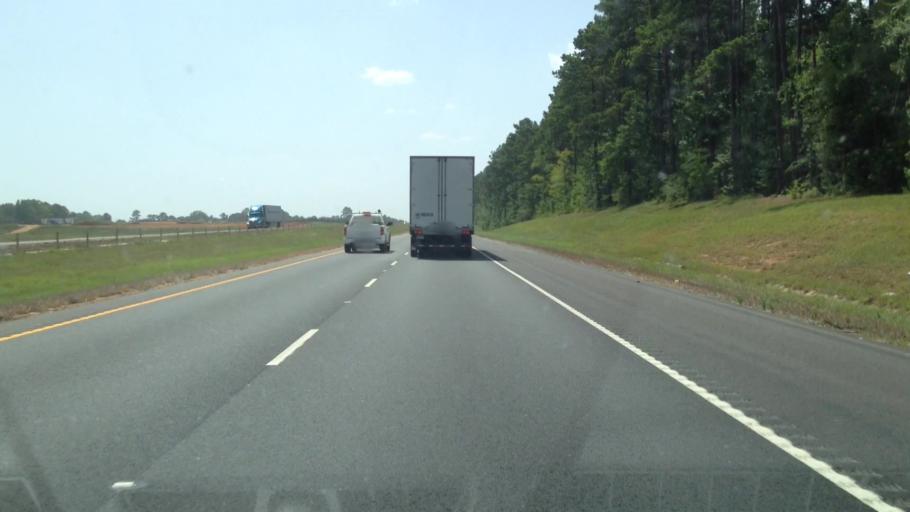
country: US
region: Louisiana
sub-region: Webster Parish
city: Minden
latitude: 32.5783
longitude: -93.2368
